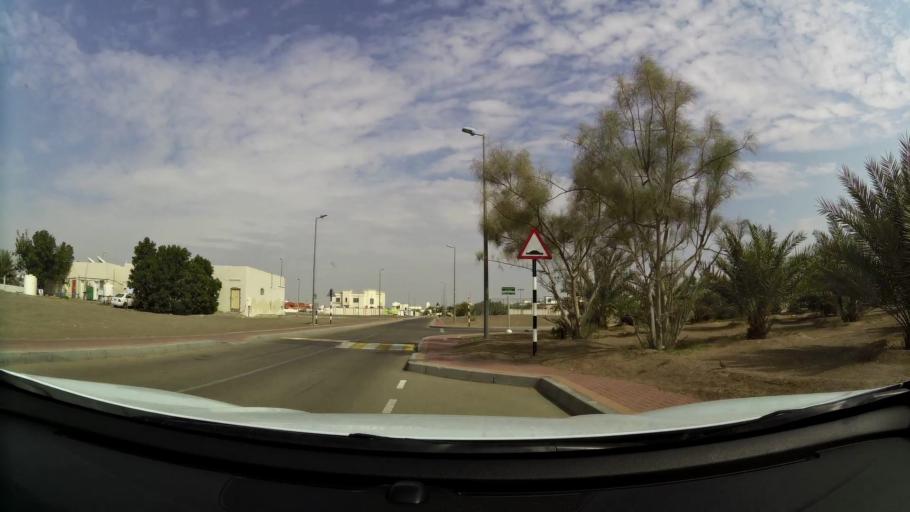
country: AE
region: Abu Dhabi
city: Al Ain
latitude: 24.0976
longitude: 55.9003
